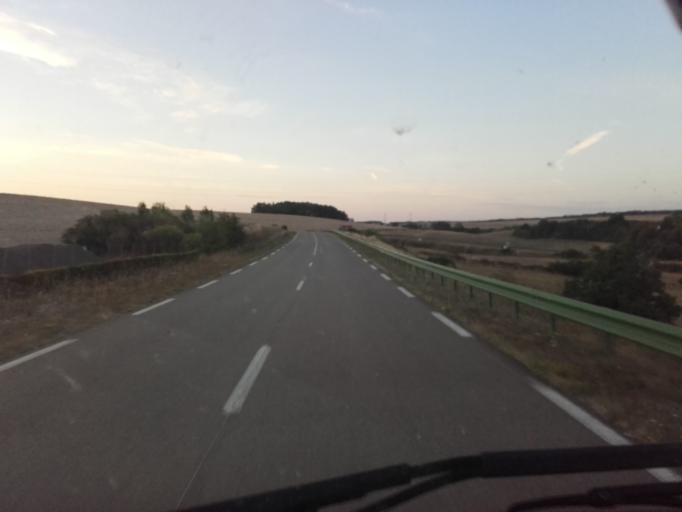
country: FR
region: Bourgogne
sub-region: Departement de l'Yonne
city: Tonnerre
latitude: 47.8388
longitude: 3.9574
